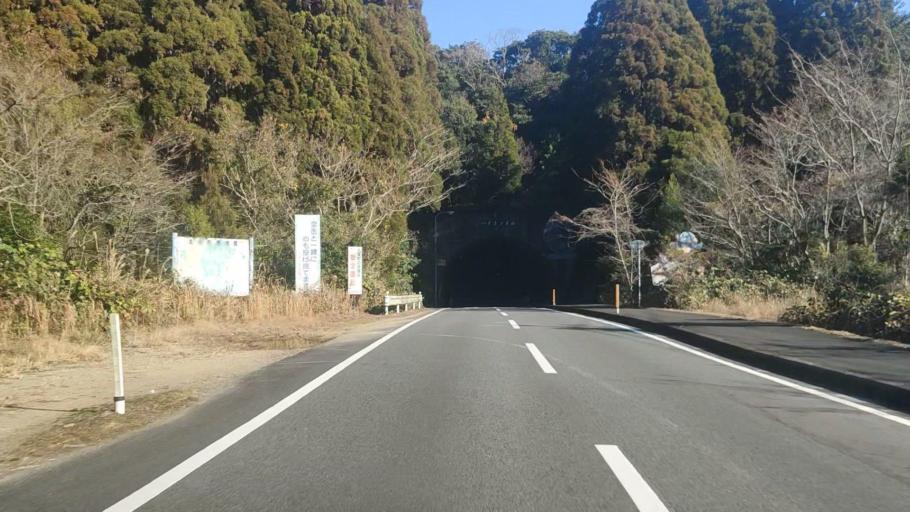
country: JP
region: Miyazaki
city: Nobeoka
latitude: 32.6973
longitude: 131.8132
